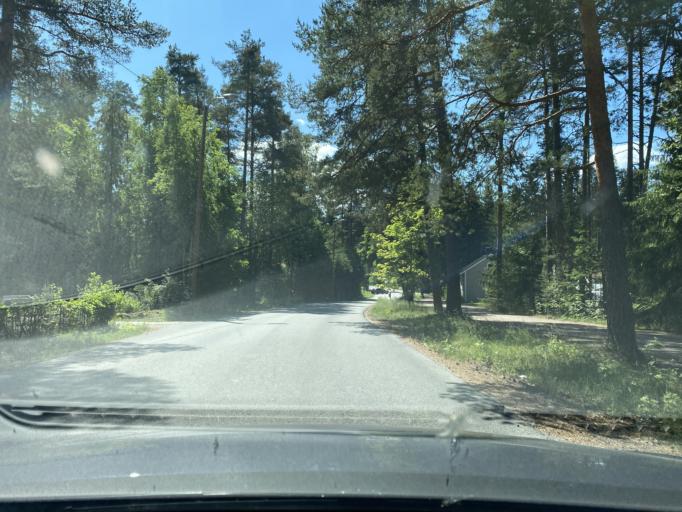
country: FI
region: Satakunta
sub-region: Rauma
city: Eura
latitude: 61.1301
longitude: 22.1660
